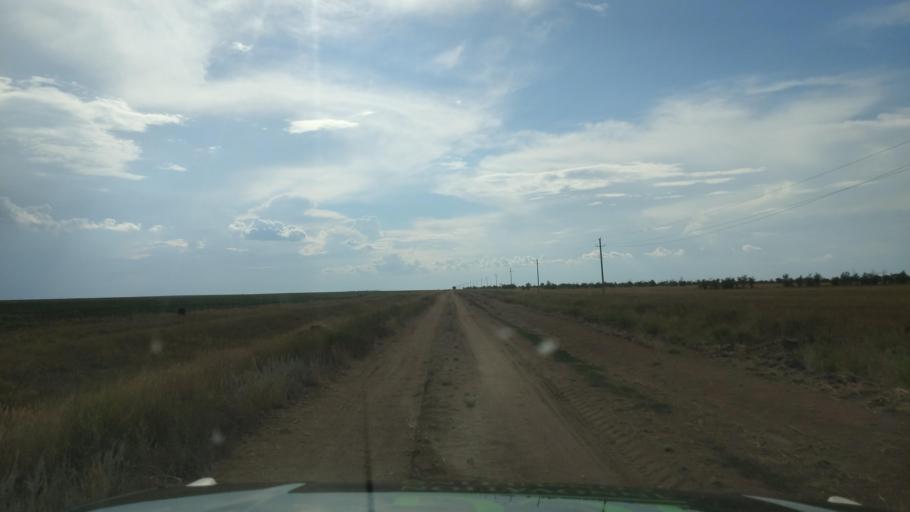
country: KZ
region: Pavlodar
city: Pavlodar
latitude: 52.5125
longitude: 77.5000
